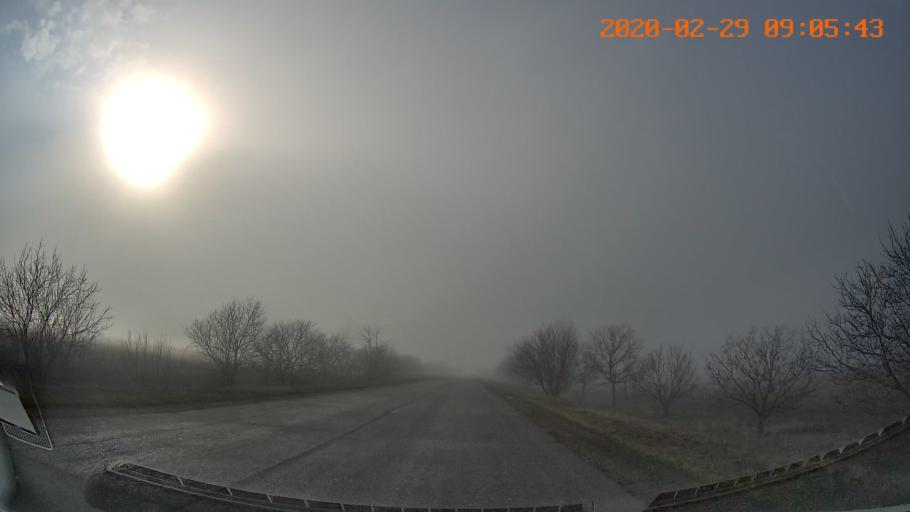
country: MD
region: Telenesti
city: Tiraspolul Nou
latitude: 46.8854
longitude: 29.7415
